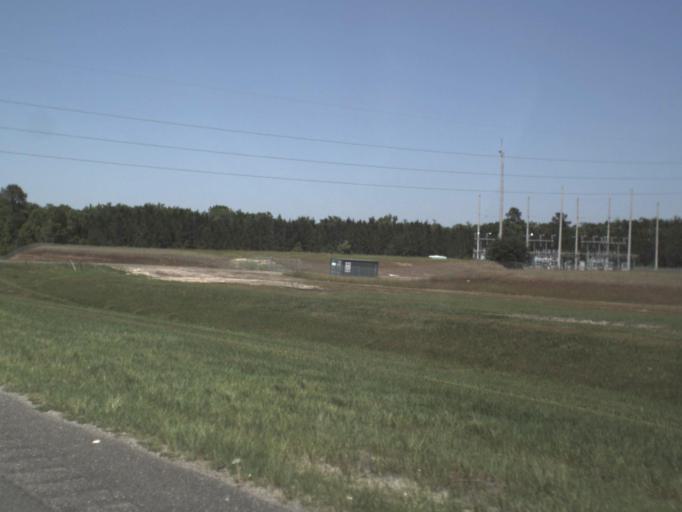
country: US
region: Florida
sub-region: Clay County
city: Lakeside
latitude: 30.1614
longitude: -81.8312
